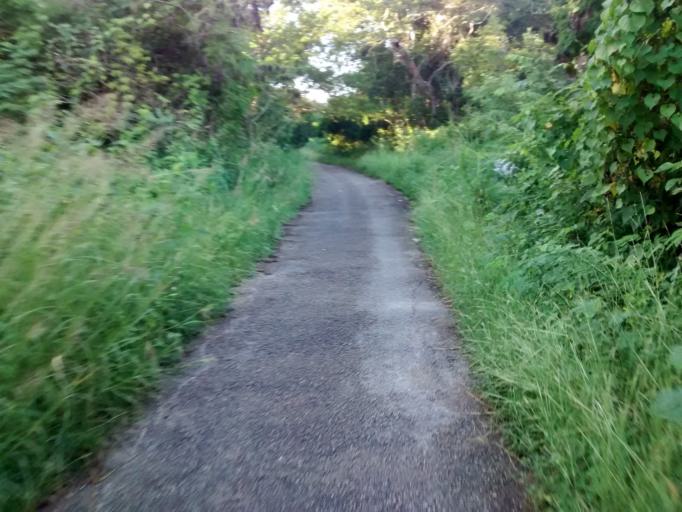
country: MX
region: Yucatan
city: Valladolid
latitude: 20.7141
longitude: -88.2204
